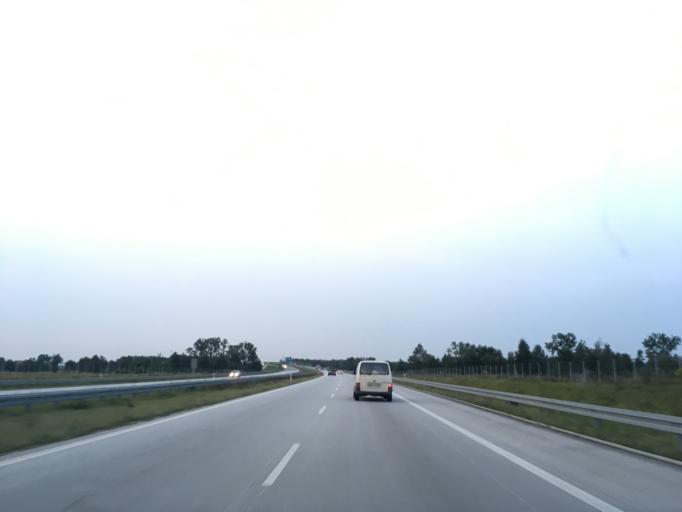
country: PL
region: Lodz Voivodeship
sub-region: Powiat lodzki wschodni
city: Andrespol
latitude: 51.7633
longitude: 19.5960
